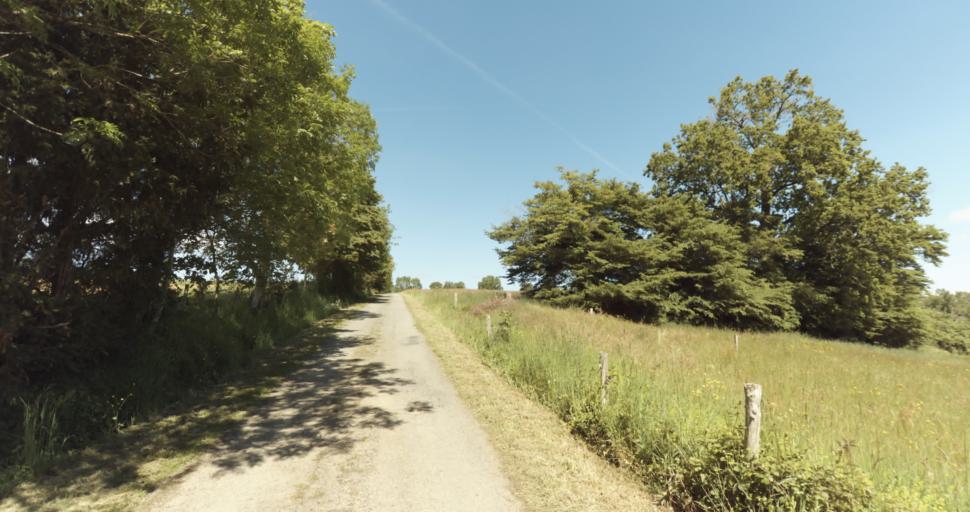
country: FR
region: Limousin
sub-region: Departement de la Haute-Vienne
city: Le Vigen
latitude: 45.7368
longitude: 1.2984
